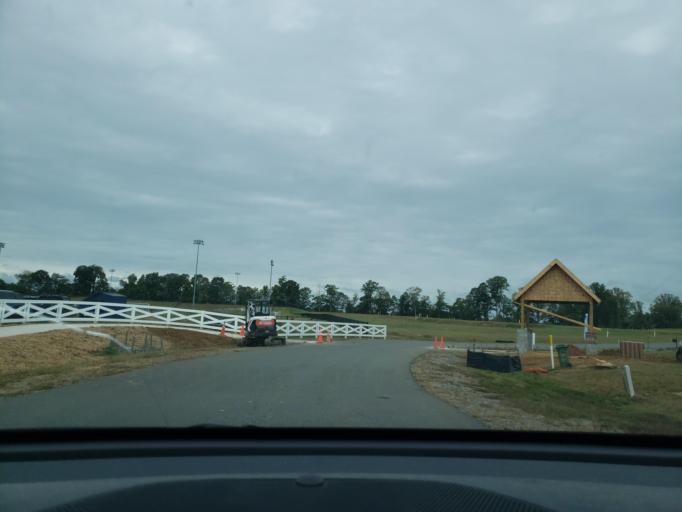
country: US
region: Virginia
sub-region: City of Fredericksburg
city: Fredericksburg
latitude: 38.2407
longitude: -77.4003
